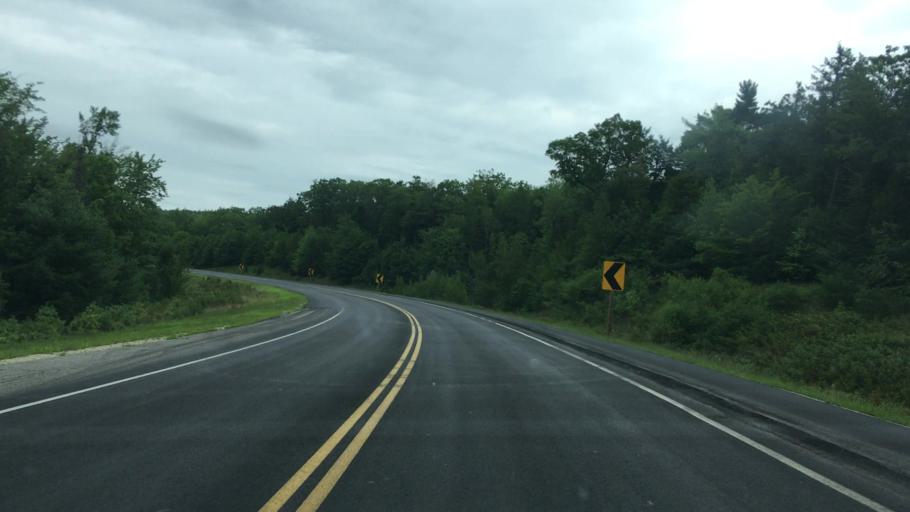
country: US
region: Maine
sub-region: Washington County
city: Cherryfield
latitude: 44.8824
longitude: -67.8583
